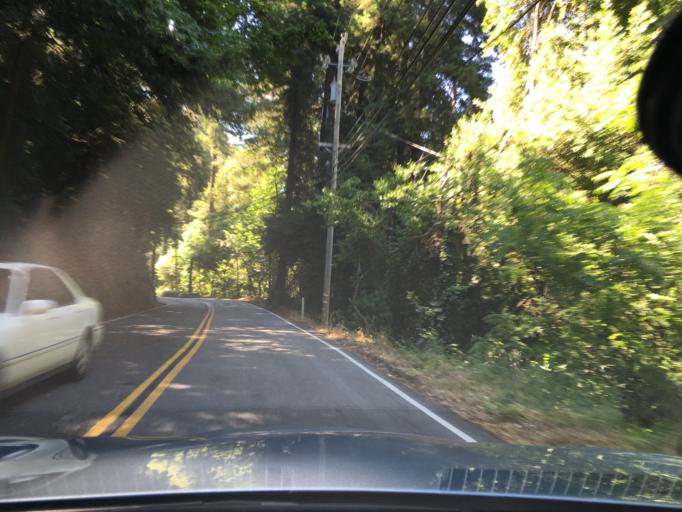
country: US
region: California
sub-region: Santa Clara County
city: Lexington Hills
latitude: 37.1598
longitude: -121.9801
